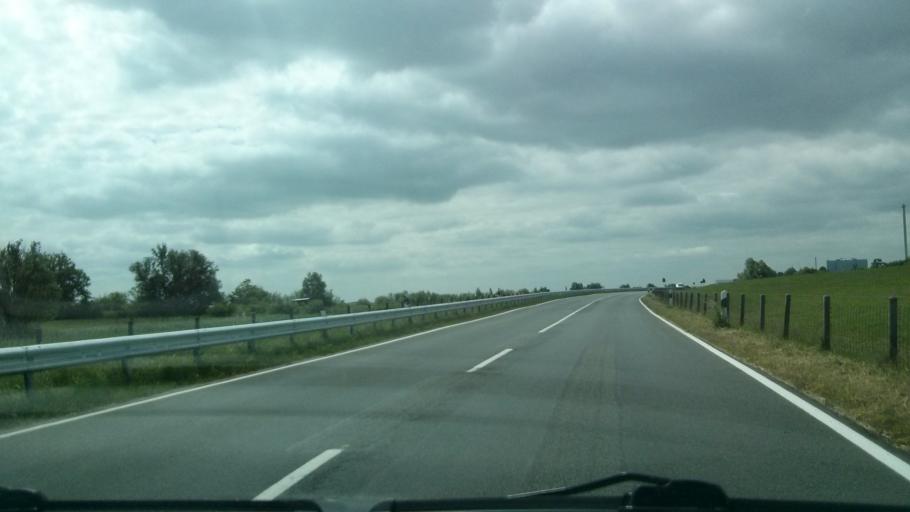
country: DE
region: Lower Saxony
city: Nordenham
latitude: 53.4387
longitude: 8.4798
